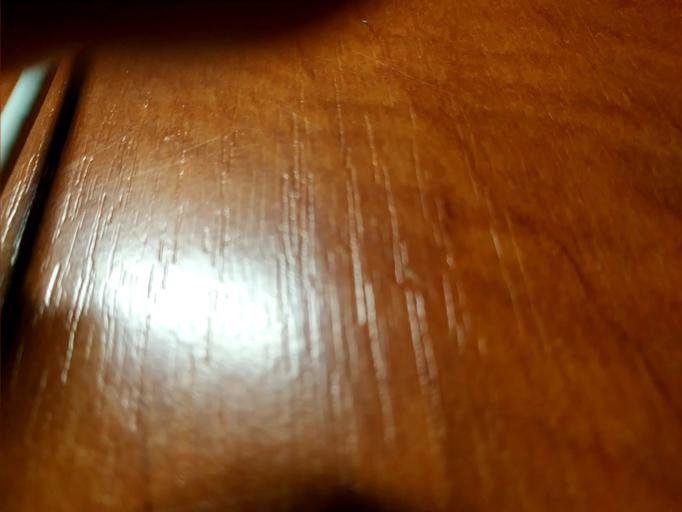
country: RU
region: Orjol
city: Naryshkino
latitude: 52.9730
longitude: 35.7075
